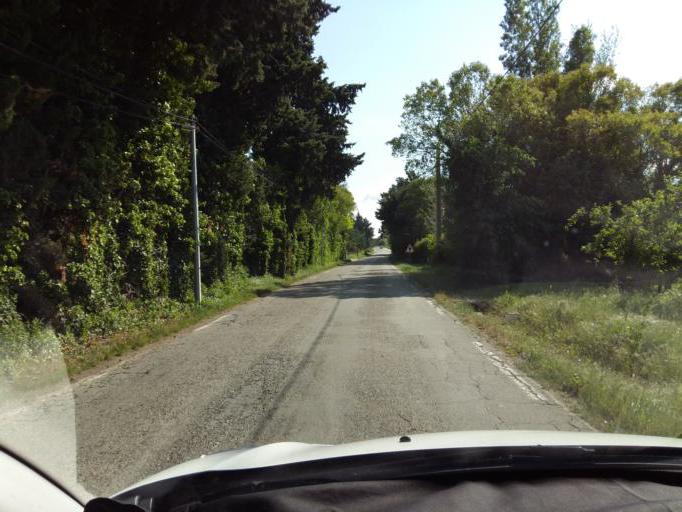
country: FR
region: Provence-Alpes-Cote d'Azur
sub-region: Departement du Vaucluse
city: Cavaillon
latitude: 43.8526
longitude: 5.0512
